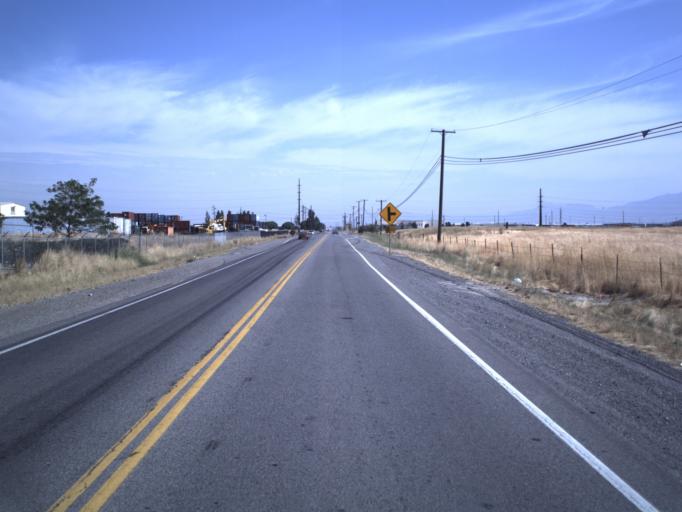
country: US
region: Utah
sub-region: Salt Lake County
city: West Valley City
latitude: 40.7439
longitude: -112.0249
